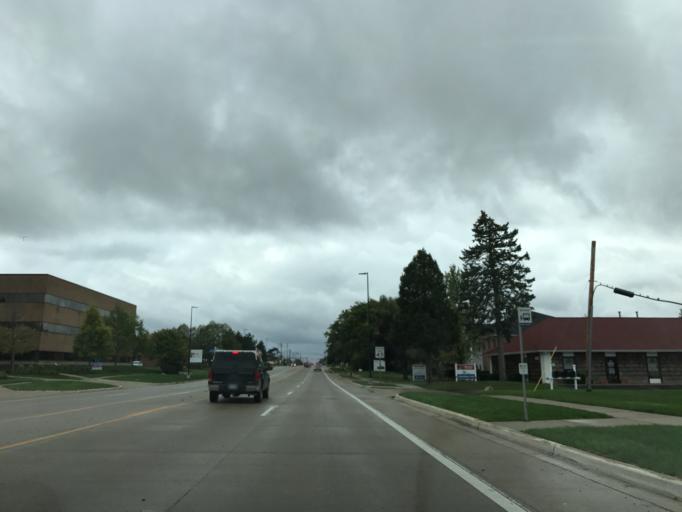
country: US
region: Michigan
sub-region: Washtenaw County
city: Ann Arbor
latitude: 42.2494
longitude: -83.6807
